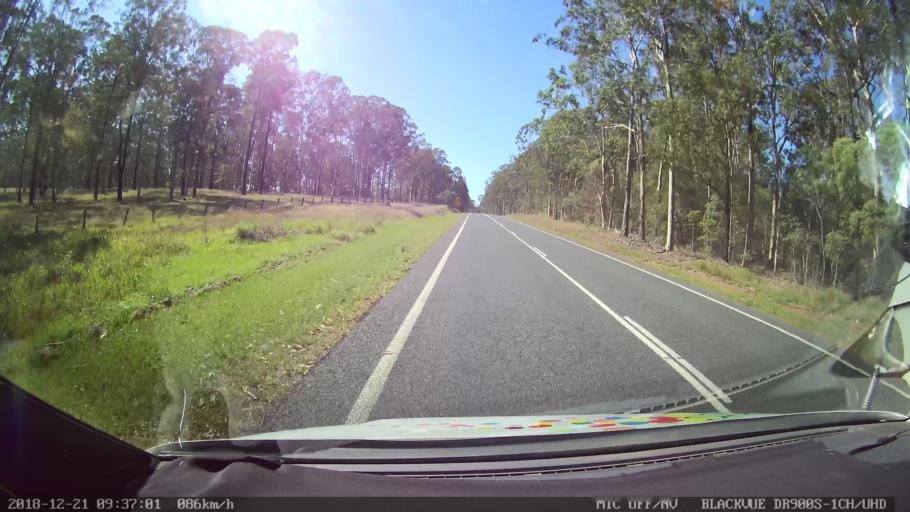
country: AU
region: New South Wales
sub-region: Clarence Valley
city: Grafton
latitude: -29.5310
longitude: 152.9852
